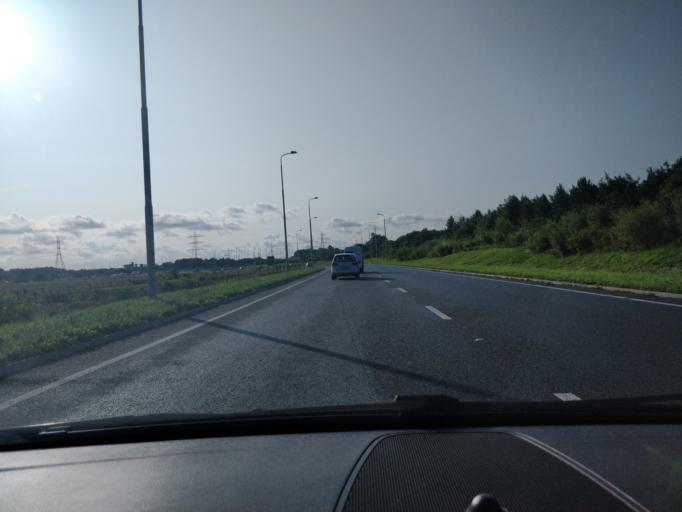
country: GB
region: England
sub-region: Sefton
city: Maghull
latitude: 53.4948
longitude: -2.9600
